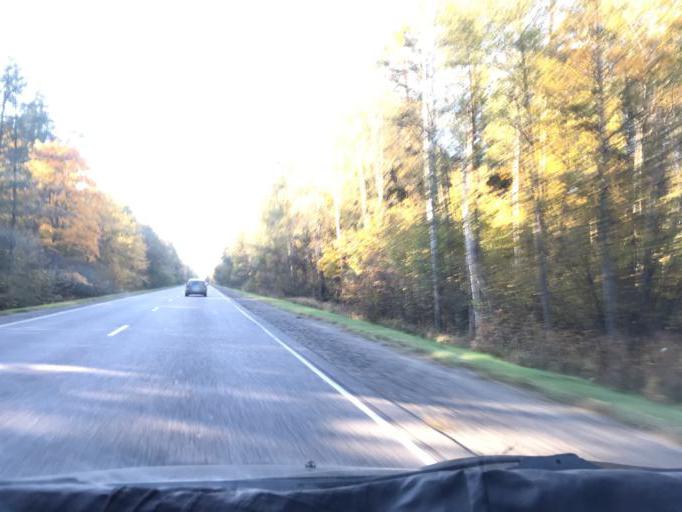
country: BY
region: Gomel
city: Pyetrykaw
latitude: 52.2622
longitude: 28.3197
